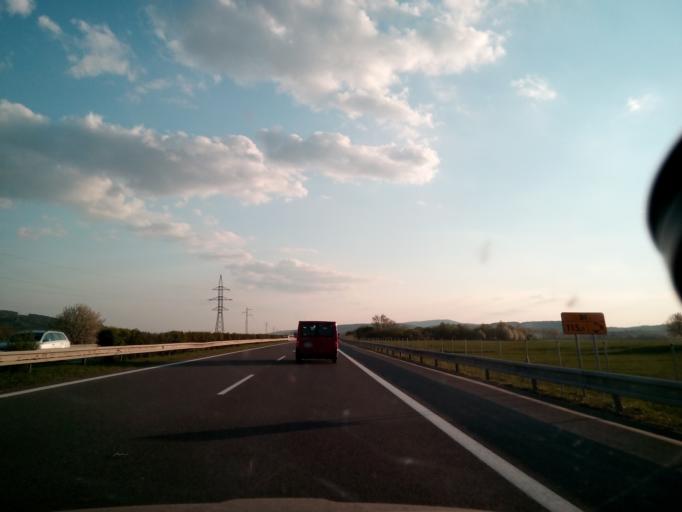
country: SK
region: Trenciansky
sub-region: Okres Trencin
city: Trencin
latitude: 48.8360
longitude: 17.9334
